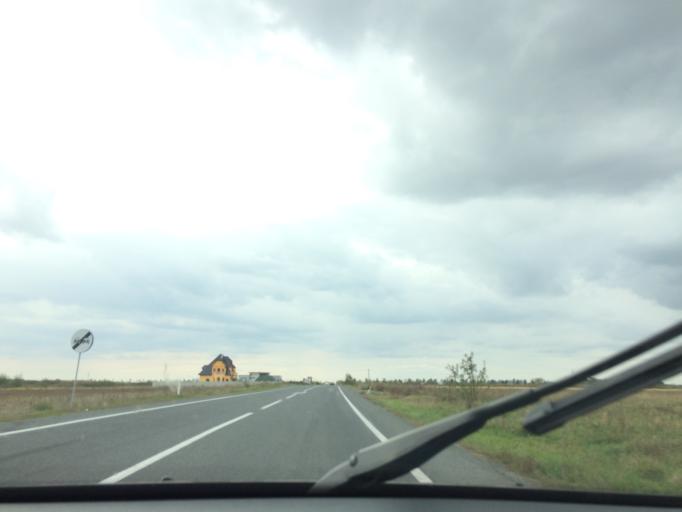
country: RO
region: Timis
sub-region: Oras Recas
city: Izvin
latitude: 45.7973
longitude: 21.4466
